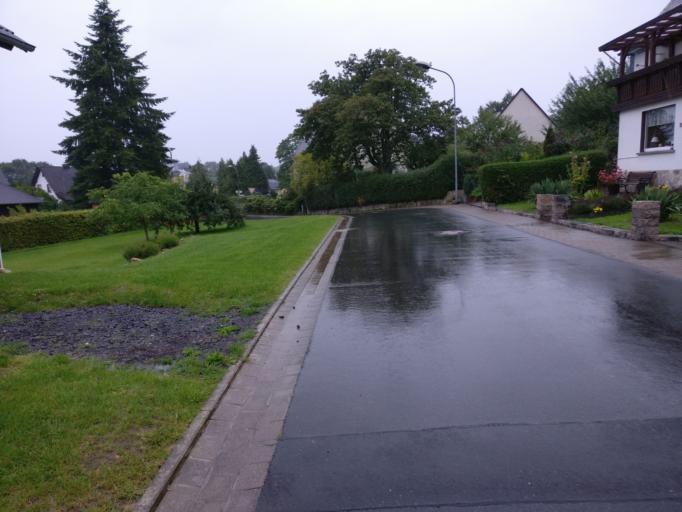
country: DE
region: Hesse
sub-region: Regierungsbezirk Giessen
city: Greifenstein
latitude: 50.6233
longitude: 8.2903
